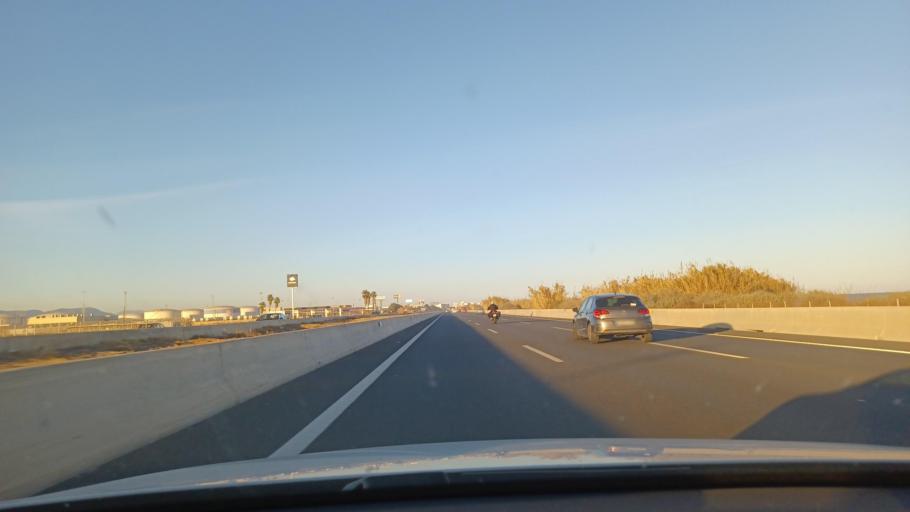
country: ES
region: Valencia
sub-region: Provincia de Valencia
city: Meliana
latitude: 39.5270
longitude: -0.3141
